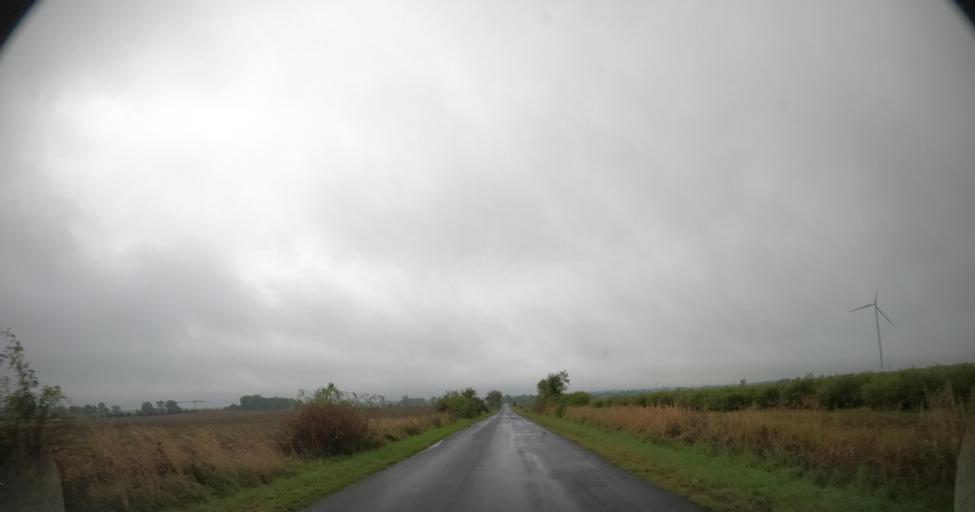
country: PL
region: West Pomeranian Voivodeship
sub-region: Powiat pyrzycki
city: Kozielice
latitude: 53.0584
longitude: 14.7801
